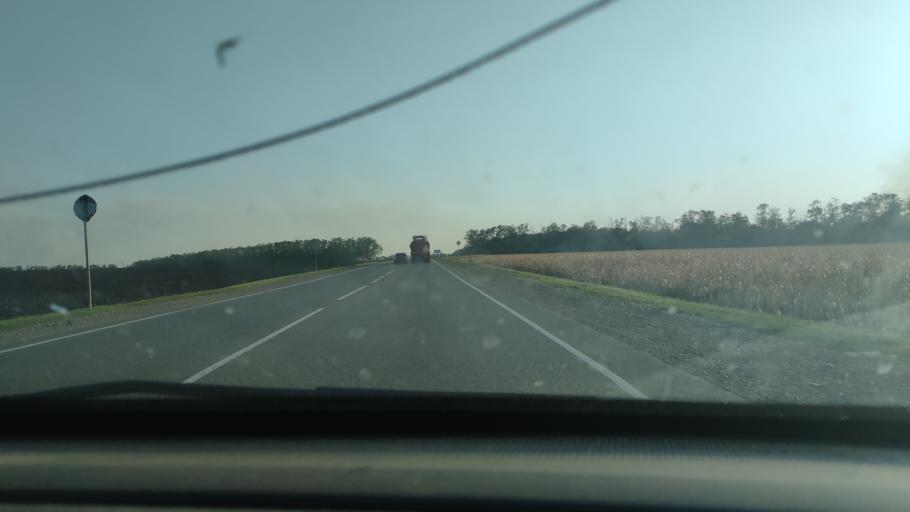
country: RU
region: Krasnodarskiy
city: Kanevskaya
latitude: 46.0421
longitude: 38.9869
